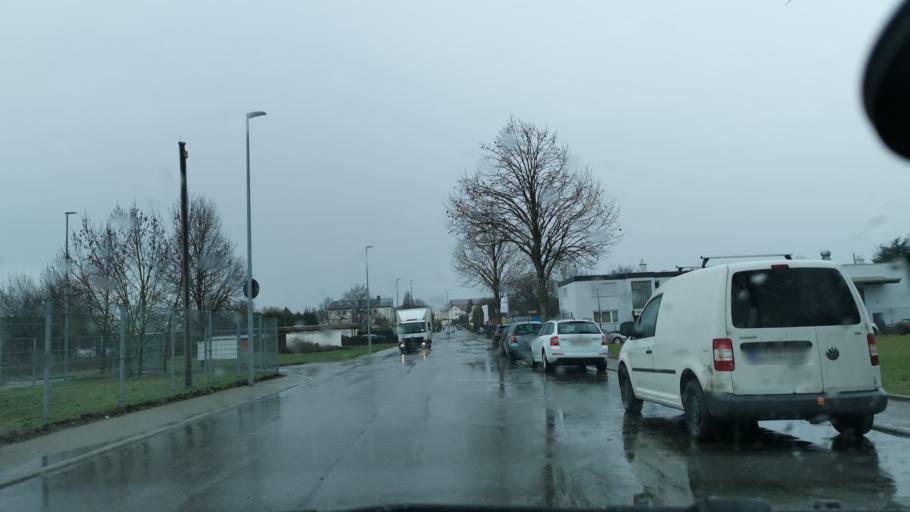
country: DE
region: Baden-Wuerttemberg
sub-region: Regierungsbezirk Stuttgart
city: Markgroningen
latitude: 48.9001
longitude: 9.0943
